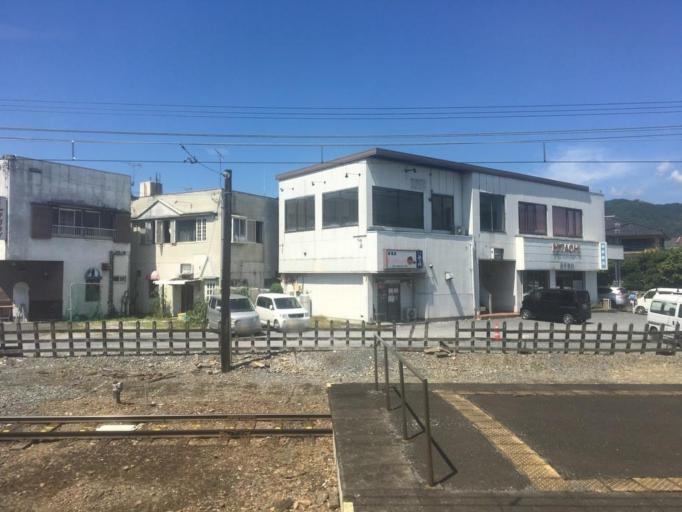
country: JP
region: Saitama
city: Chichibu
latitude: 36.0682
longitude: 139.0940
